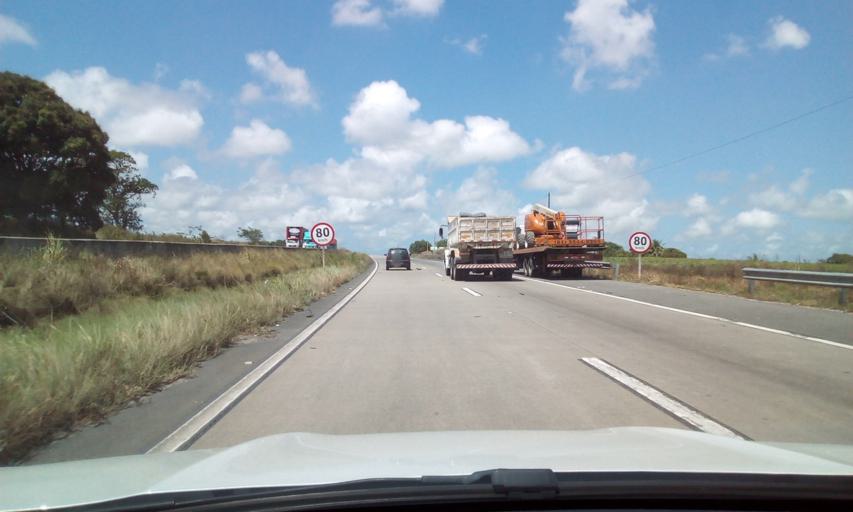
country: BR
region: Pernambuco
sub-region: Itapissuma
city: Itapissuma
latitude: -7.7073
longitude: -34.9271
